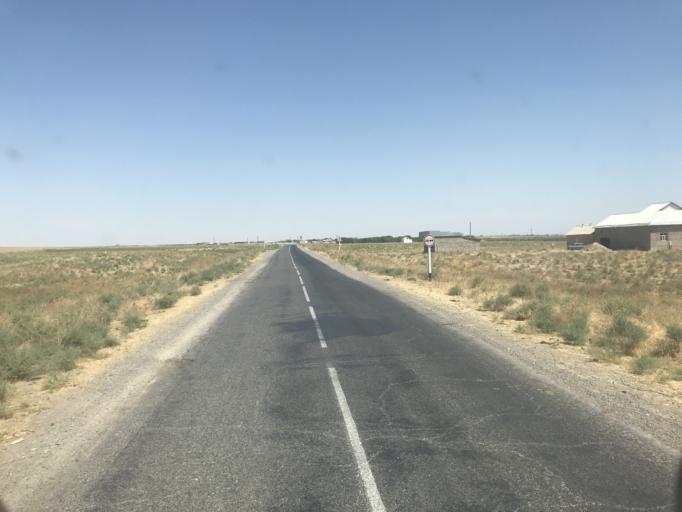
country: UZ
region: Toshkent
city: Yangiyul
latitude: 41.3799
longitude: 68.7582
